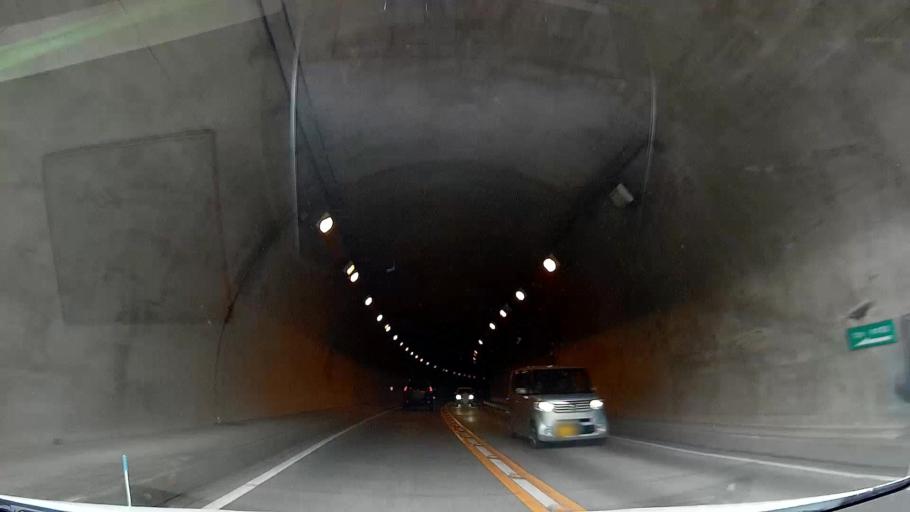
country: JP
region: Shizuoka
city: Ito
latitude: 35.0187
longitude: 139.0958
